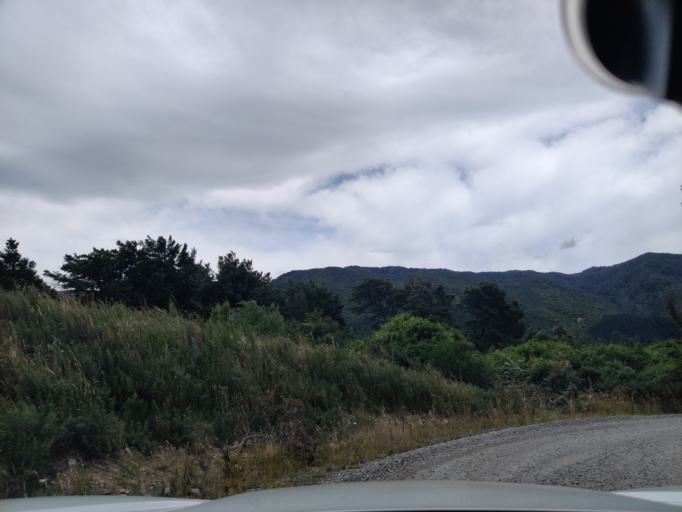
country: NZ
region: Wellington
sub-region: Masterton District
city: Masterton
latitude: -41.0395
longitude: 175.4033
